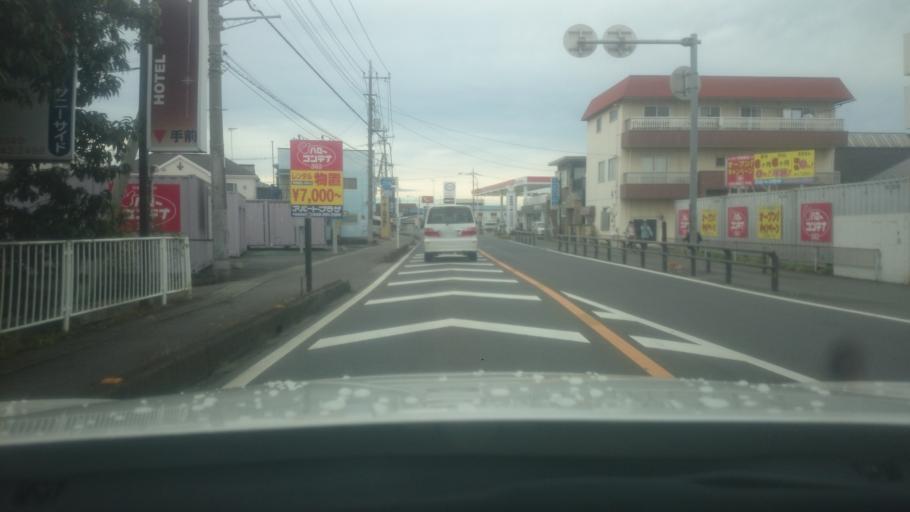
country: JP
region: Saitama
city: Kamifukuoka
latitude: 35.8747
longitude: 139.5022
